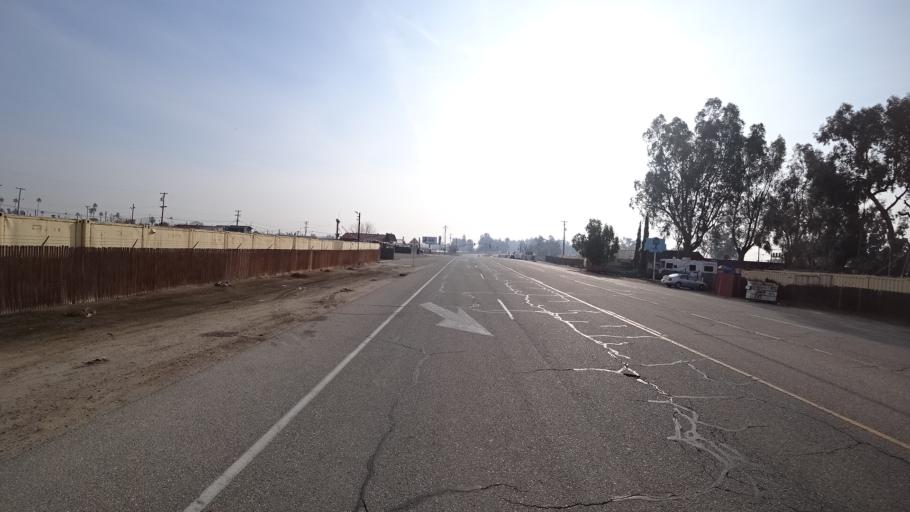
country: US
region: California
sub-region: Kern County
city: Oildale
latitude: 35.4042
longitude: -119.0426
